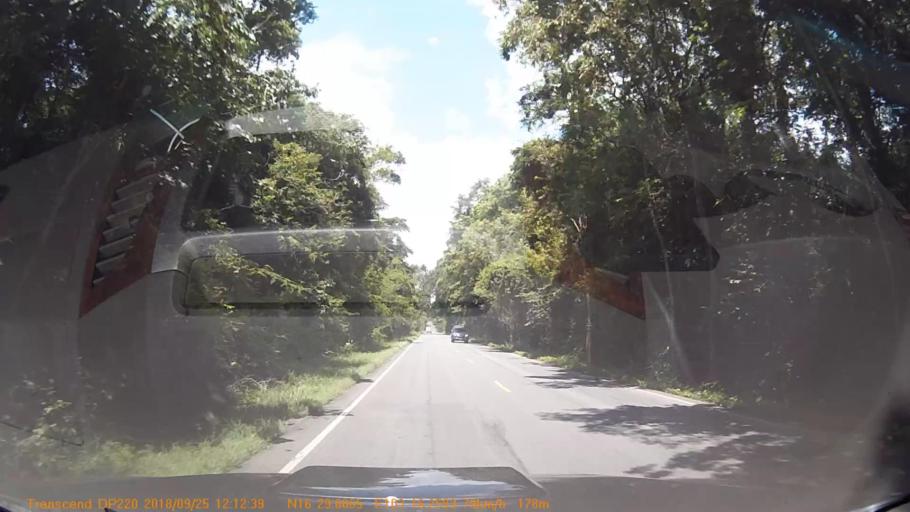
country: TH
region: Kalasin
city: Huai Mek
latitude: 16.4947
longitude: 103.2710
